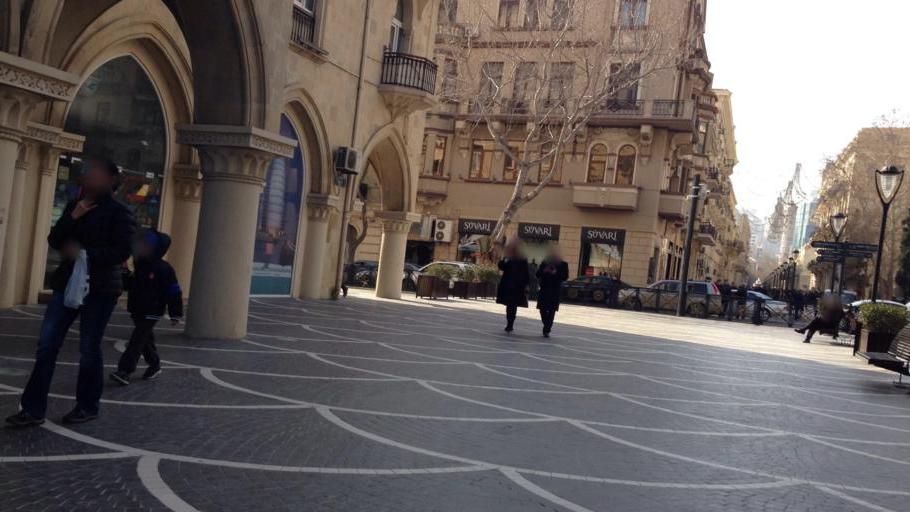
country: AZ
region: Baki
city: Baku
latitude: 40.3737
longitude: 49.8427
